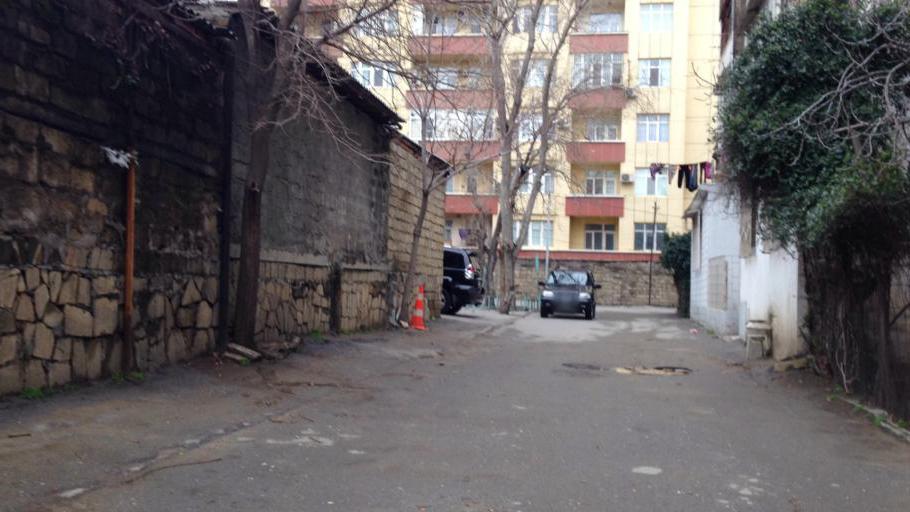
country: AZ
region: Baki
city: Baku
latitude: 40.3898
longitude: 49.8525
